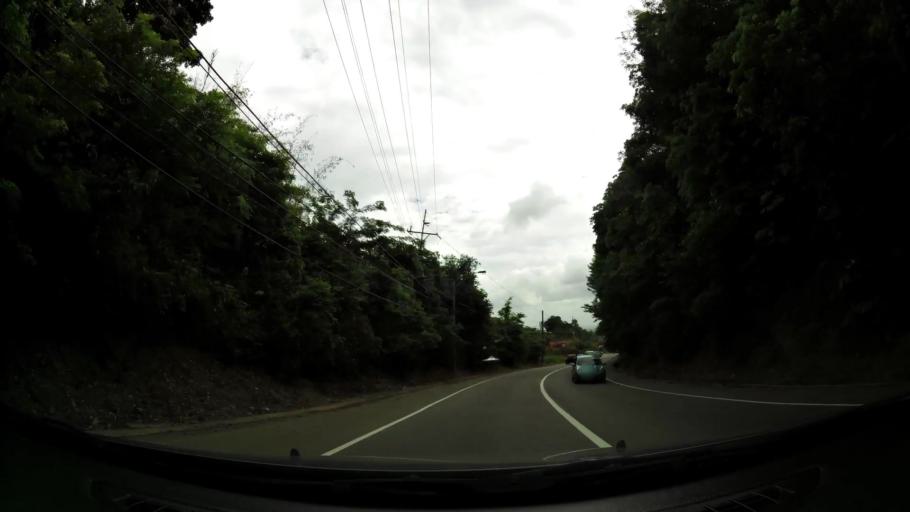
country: TT
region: San Juan/Laventille
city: Laventille
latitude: 10.6678
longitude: -61.4849
